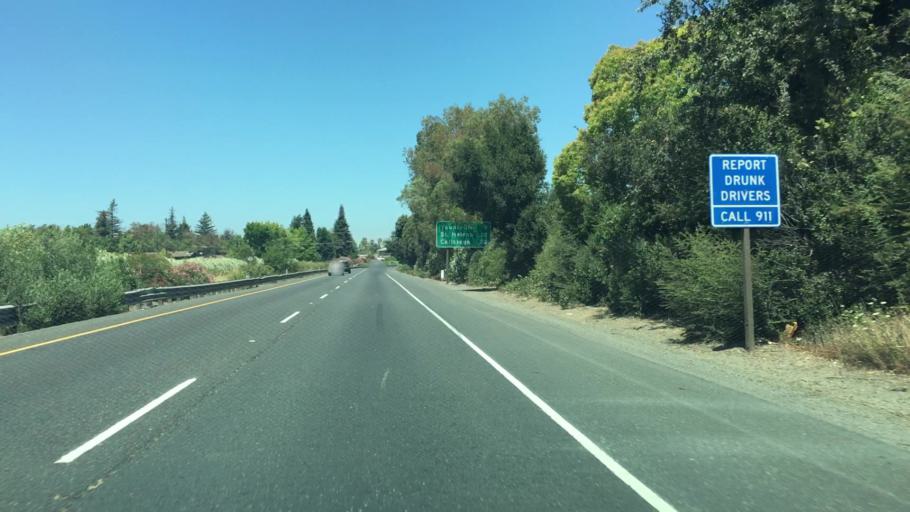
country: US
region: California
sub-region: Napa County
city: Napa
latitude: 38.2894
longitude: -122.3014
